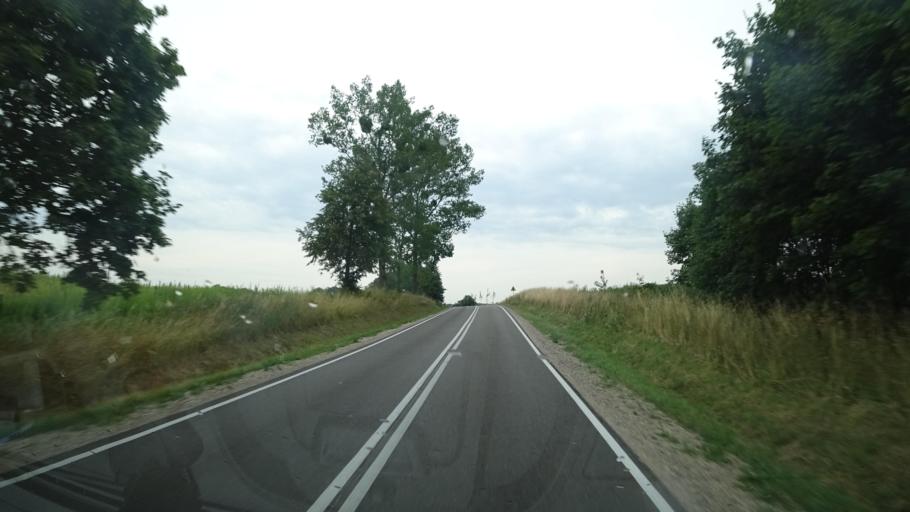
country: PL
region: Warmian-Masurian Voivodeship
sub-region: Powiat gizycki
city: Ryn
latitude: 53.9372
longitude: 21.5232
